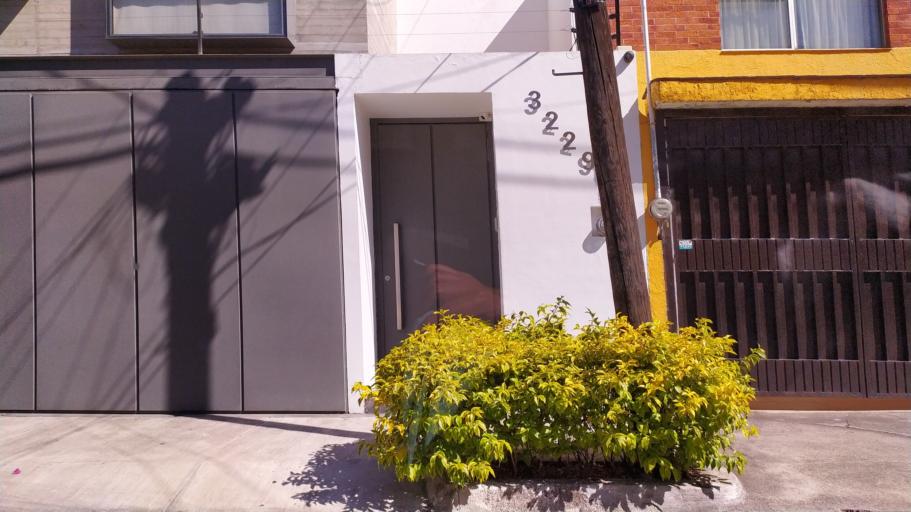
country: MX
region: Jalisco
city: Zapopan2
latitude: 20.6960
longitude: -103.3917
